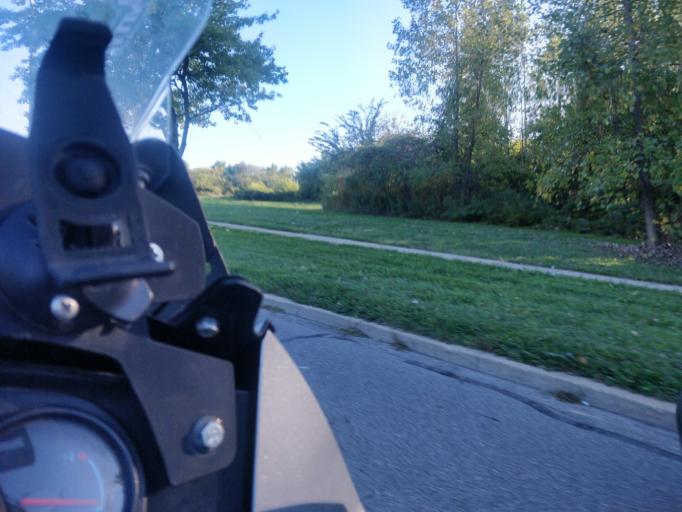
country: US
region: Michigan
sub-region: Wayne County
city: Lincoln Park
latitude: 42.2663
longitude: -83.1759
